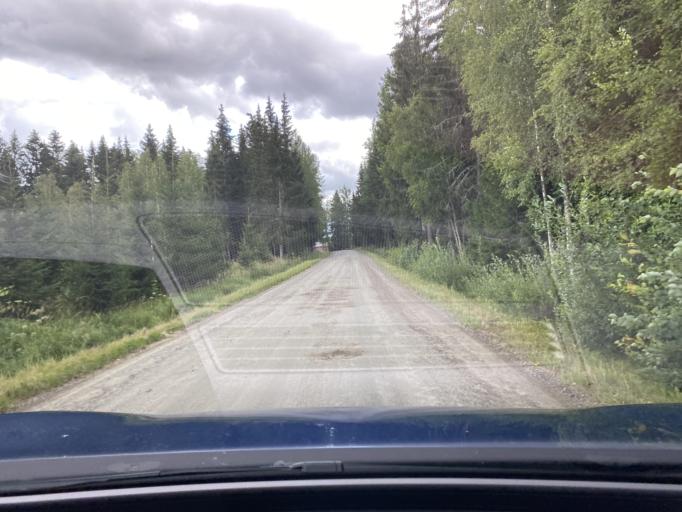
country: FI
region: Pirkanmaa
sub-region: Lounais-Pirkanmaa
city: Punkalaidun
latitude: 61.2191
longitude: 23.1655
